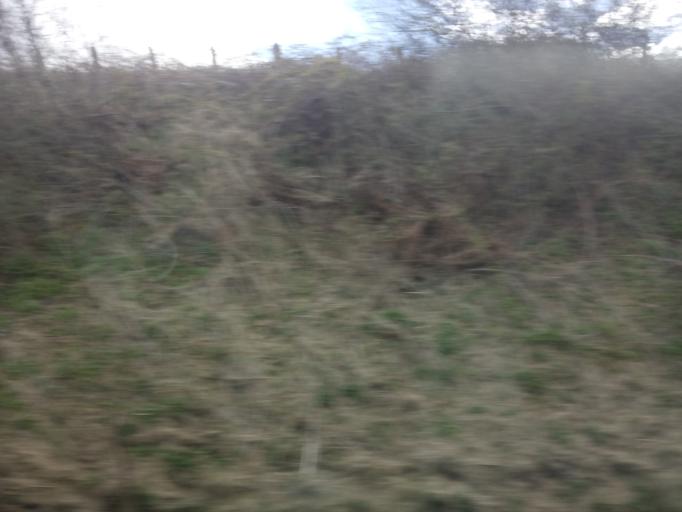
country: GB
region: Scotland
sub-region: The Scottish Borders
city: Chirnside
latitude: 55.8670
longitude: -2.2603
